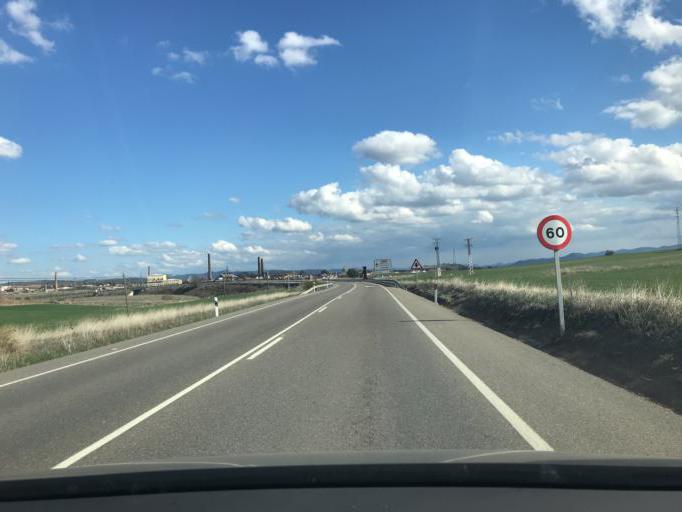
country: ES
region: Andalusia
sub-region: Province of Cordoba
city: Penarroya-Pueblonuevo
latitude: 38.2951
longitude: -5.2865
